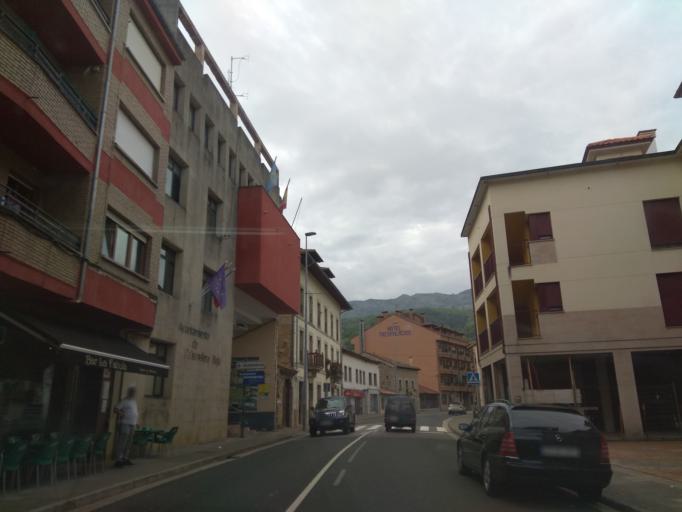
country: ES
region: Cantabria
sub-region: Provincia de Cantabria
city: Tresviso
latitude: 43.3251
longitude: -4.5837
